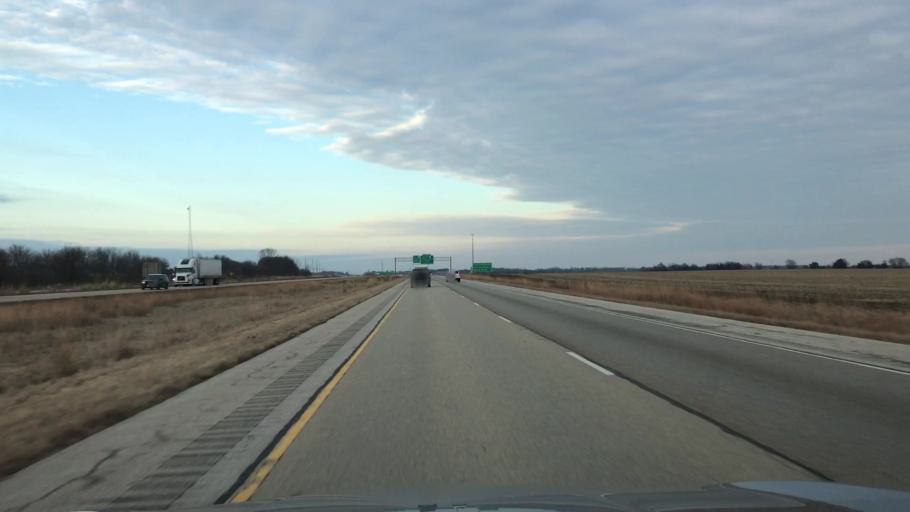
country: US
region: Illinois
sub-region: McLean County
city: Bloomington
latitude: 40.4224
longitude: -89.0426
